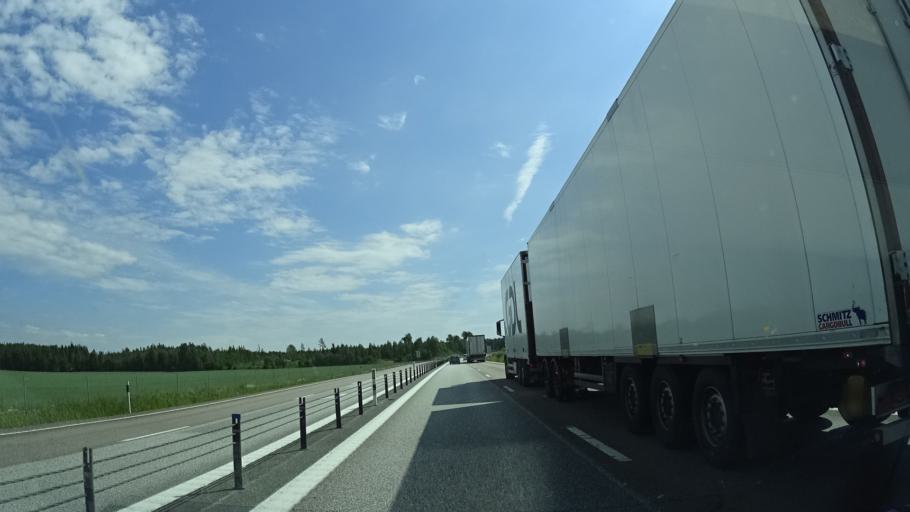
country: SE
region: Vaermland
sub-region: Kristinehamns Kommun
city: Kristinehamn
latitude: 59.3791
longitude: 13.9083
